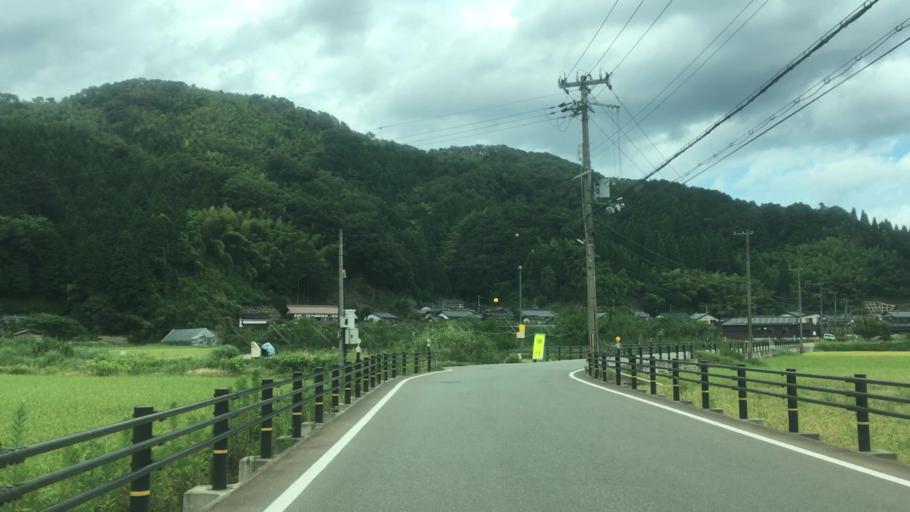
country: JP
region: Hyogo
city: Toyooka
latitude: 35.5907
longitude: 134.7983
